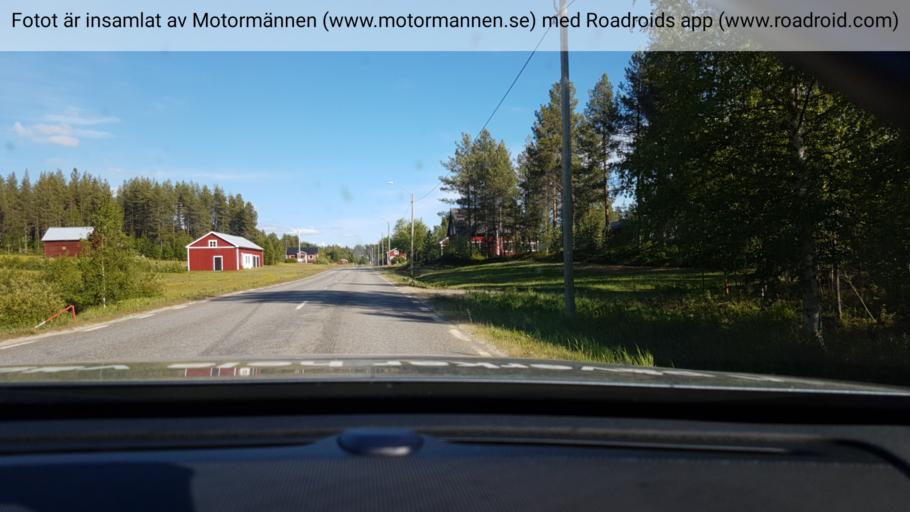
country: SE
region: Vaesterbotten
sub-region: Lycksele Kommun
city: Lycksele
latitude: 64.7636
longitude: 19.0540
